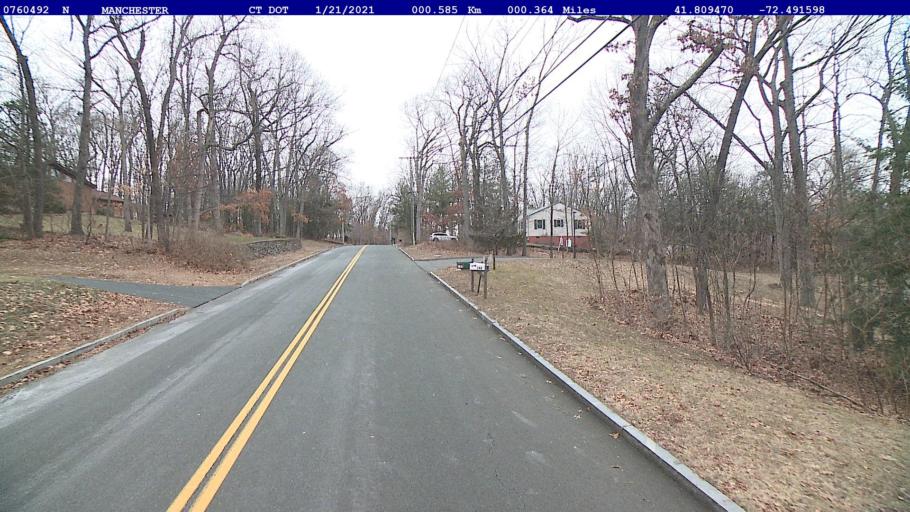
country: US
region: Connecticut
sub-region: Hartford County
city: Manchester
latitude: 41.8095
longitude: -72.4916
